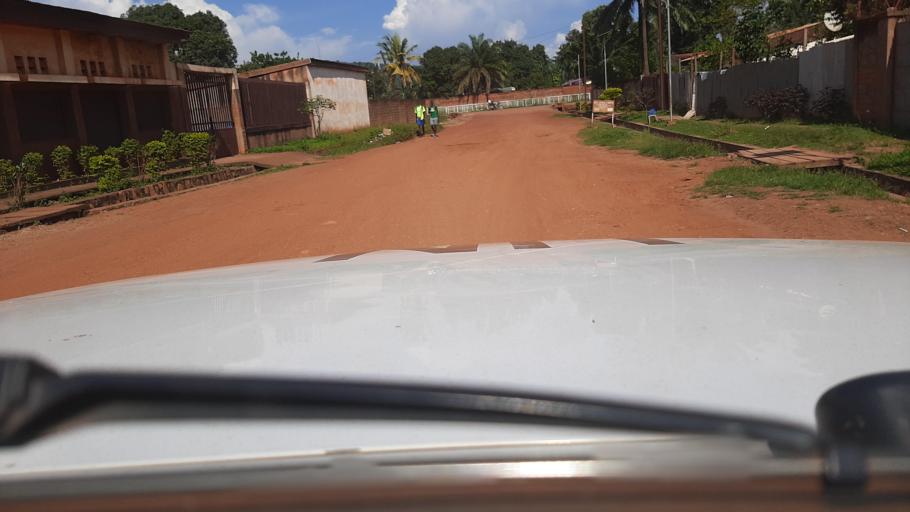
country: CF
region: Bangui
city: Bangui
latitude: 4.3739
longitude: 18.5520
